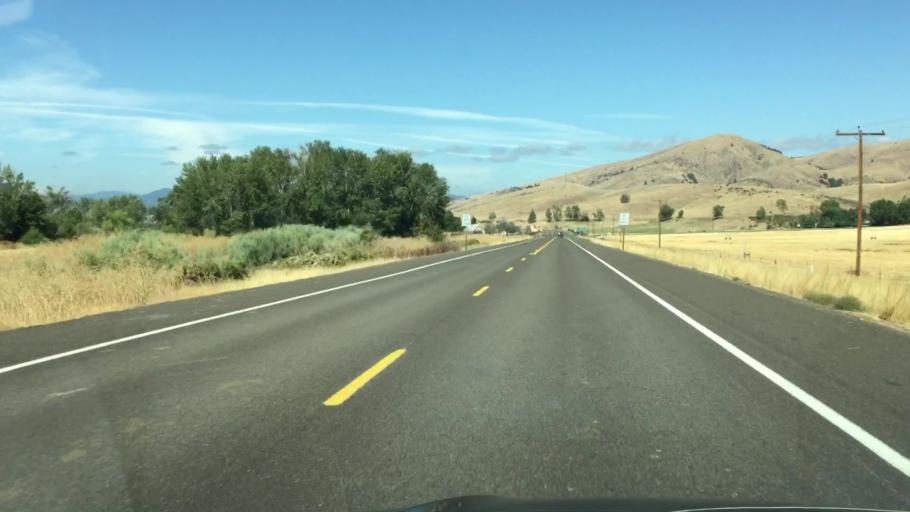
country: US
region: Oregon
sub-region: Wasco County
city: The Dalles
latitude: 45.2494
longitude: -121.1680
